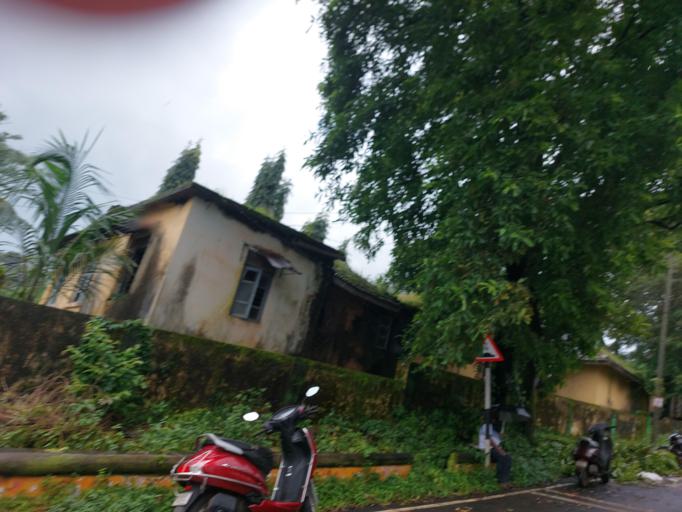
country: IN
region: Goa
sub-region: North Goa
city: Valpoy
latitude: 15.5288
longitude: 74.1317
